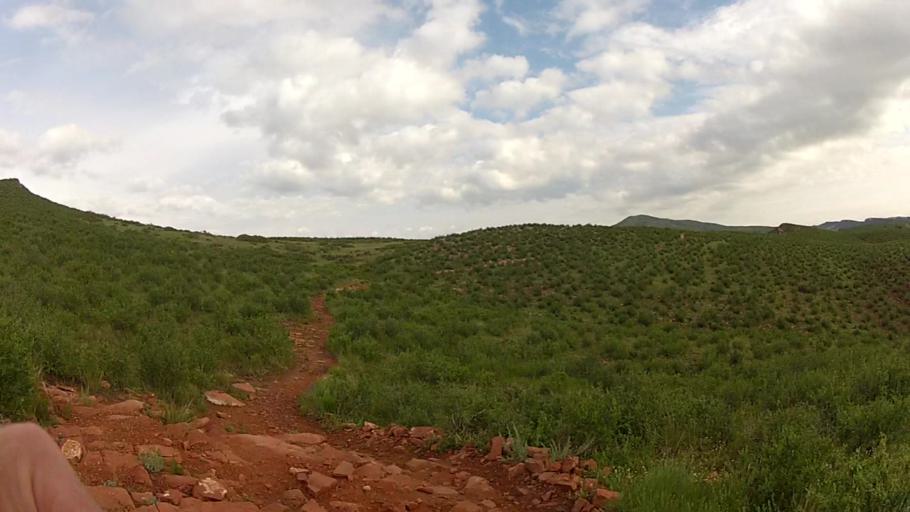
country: US
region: Colorado
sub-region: Larimer County
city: Loveland
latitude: 40.4374
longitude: -105.1563
